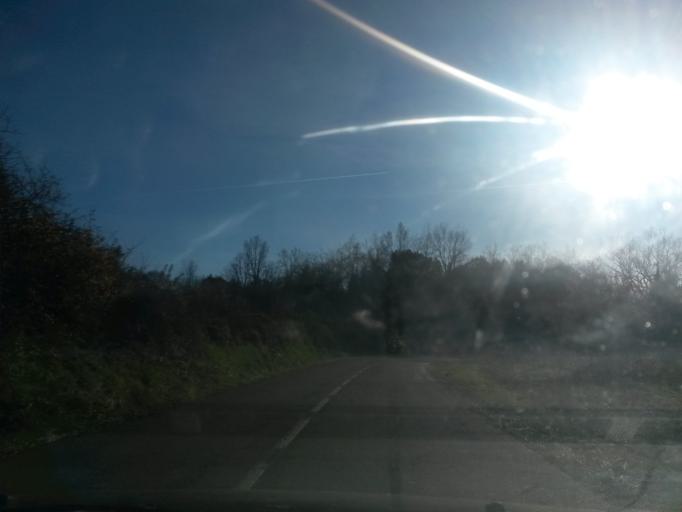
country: ES
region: Catalonia
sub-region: Provincia de Girona
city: Sant Gregori
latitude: 42.0275
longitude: 2.6754
